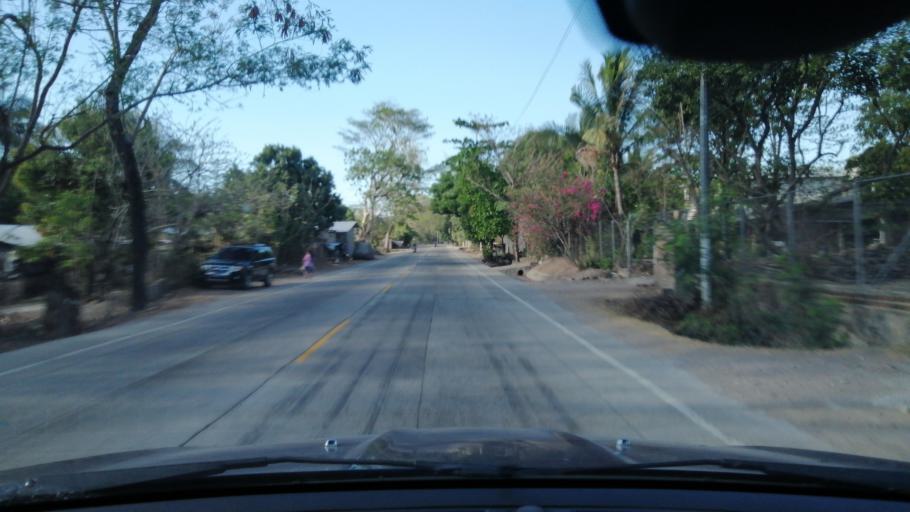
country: SV
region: Santa Ana
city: Texistepeque
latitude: 14.2011
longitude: -89.4960
